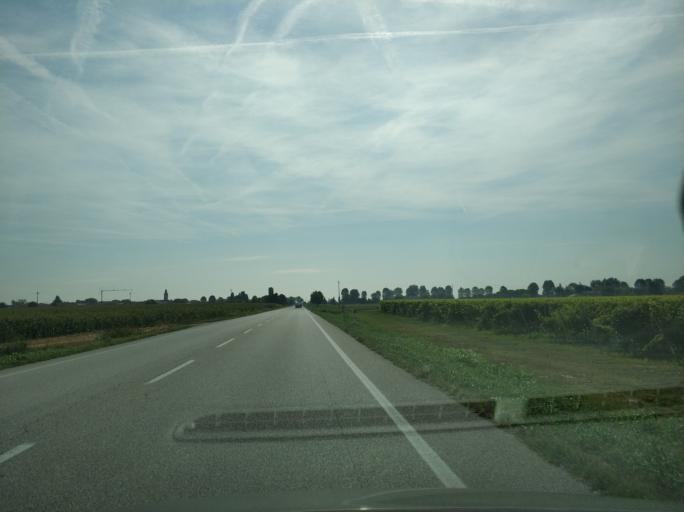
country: IT
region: Veneto
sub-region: Provincia di Venezia
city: Pegolotte
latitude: 45.2134
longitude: 12.0226
